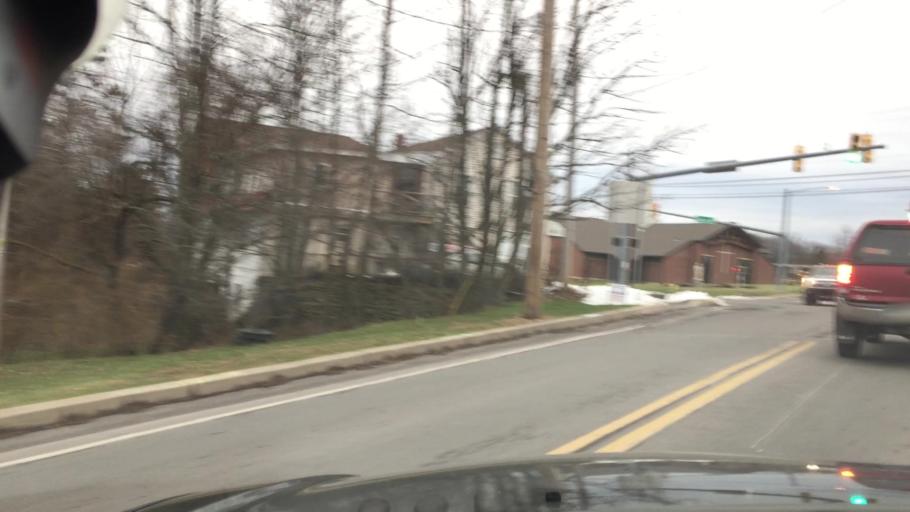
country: US
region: Pennsylvania
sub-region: Luzerne County
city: Mountain Top
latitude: 41.1201
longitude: -75.9105
